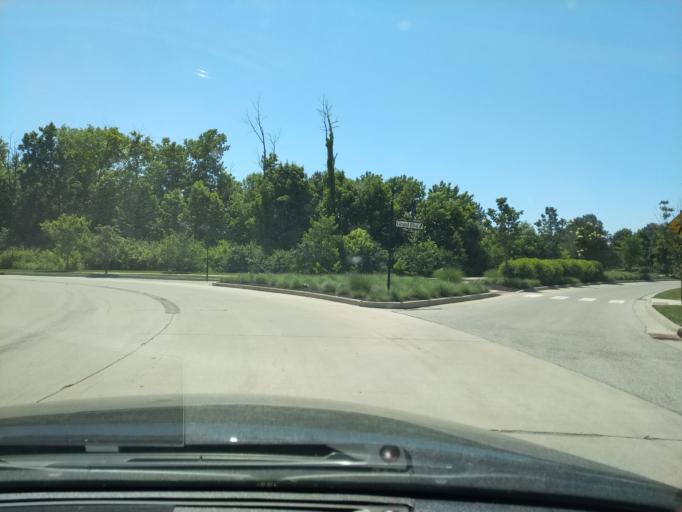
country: US
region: Indiana
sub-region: Hamilton County
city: Carmel
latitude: 39.9740
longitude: -86.1499
